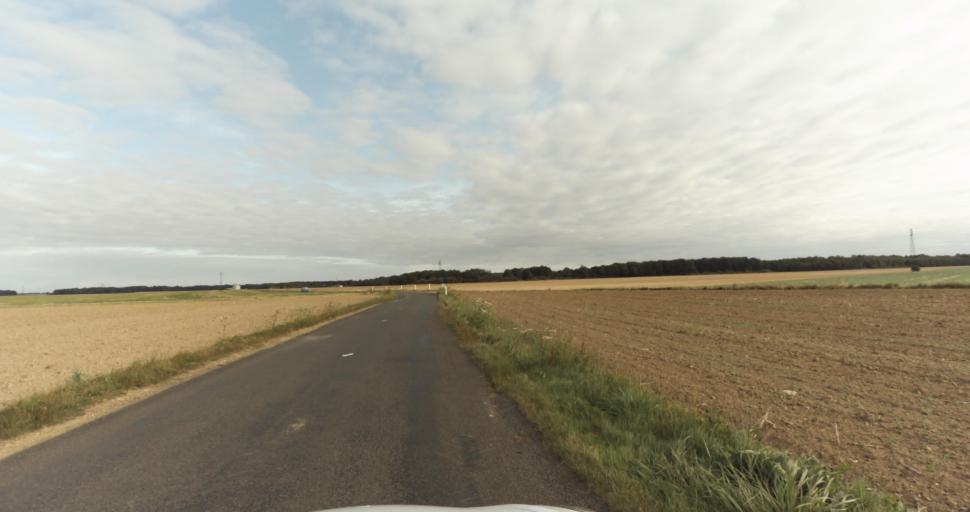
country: FR
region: Centre
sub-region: Departement d'Eure-et-Loir
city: Vert-en-Drouais
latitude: 48.7817
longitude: 1.2951
